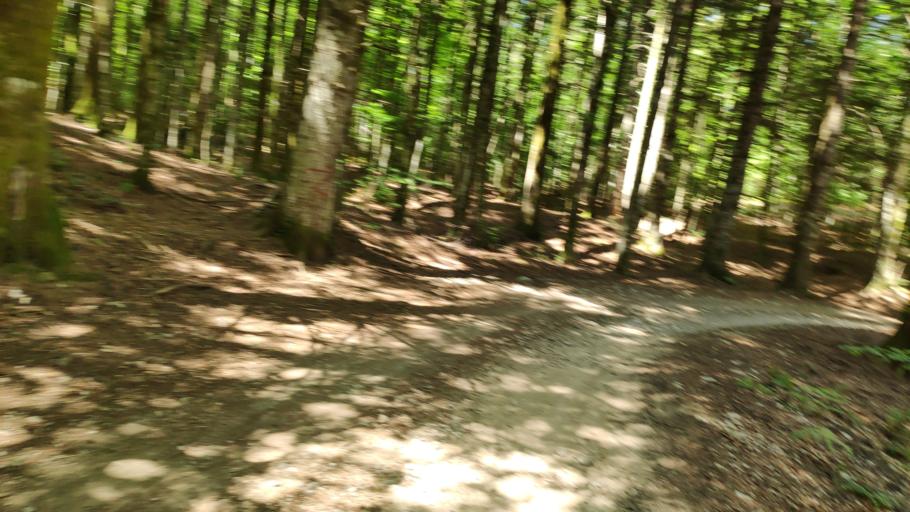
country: IT
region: Calabria
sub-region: Provincia di Vibo-Valentia
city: Mongiana
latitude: 38.5342
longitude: 16.3776
